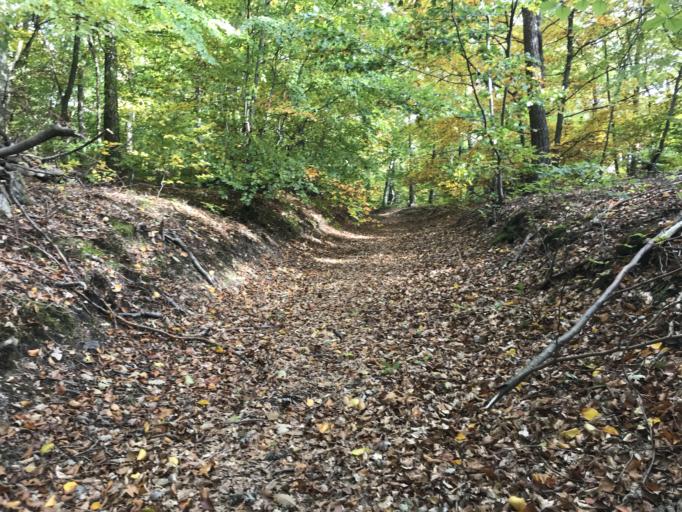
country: DE
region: Rheinland-Pfalz
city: Dannenfels
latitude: 49.6582
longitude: 7.9722
